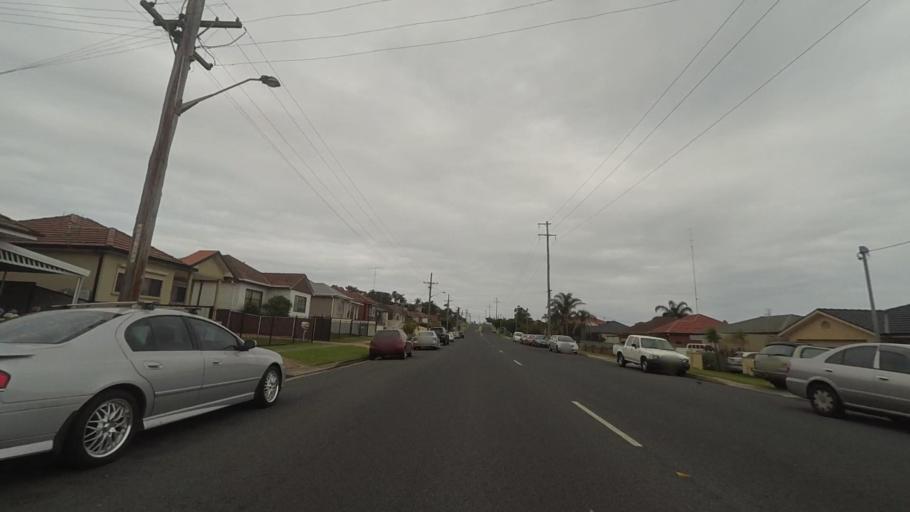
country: AU
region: New South Wales
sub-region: Wollongong
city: Port Kembla
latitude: -34.4880
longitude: 150.8966
